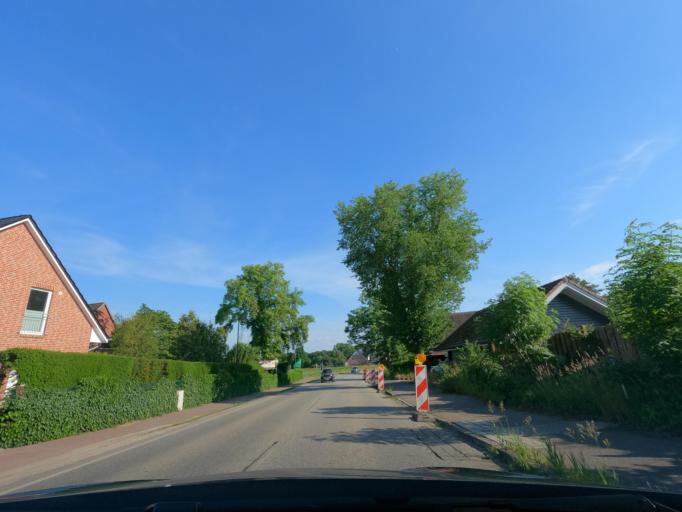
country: DE
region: Schleswig-Holstein
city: Gross Nordende
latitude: 53.7024
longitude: 9.6493
